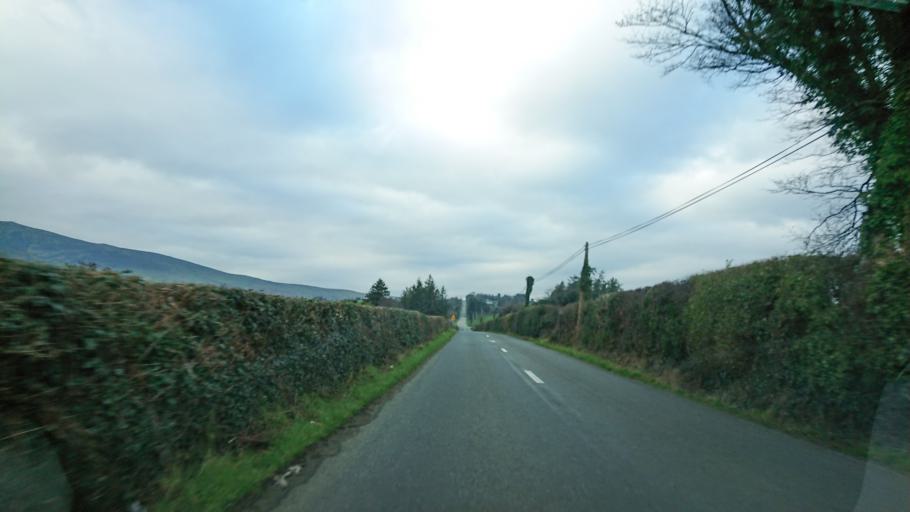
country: IE
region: Munster
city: Carrick-on-Suir
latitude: 52.3176
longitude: -7.5481
